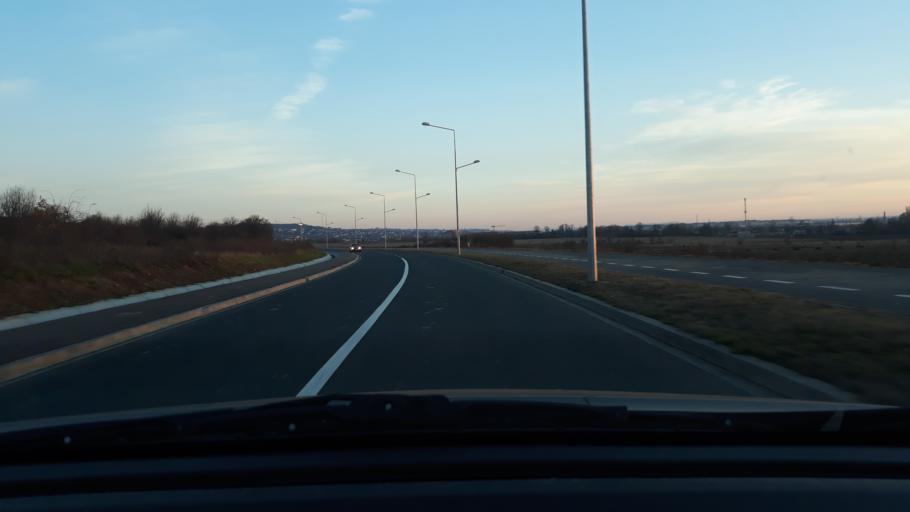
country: RO
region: Bihor
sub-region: Comuna Biharea
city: Oradea
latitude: 47.1039
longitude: 21.9086
